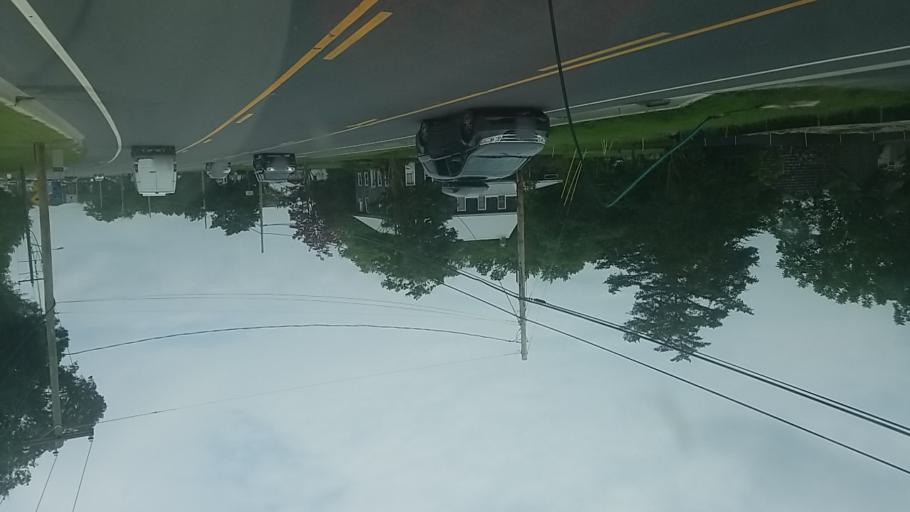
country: US
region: Delaware
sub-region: Sussex County
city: Ocean View
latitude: 38.5489
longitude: -75.1211
